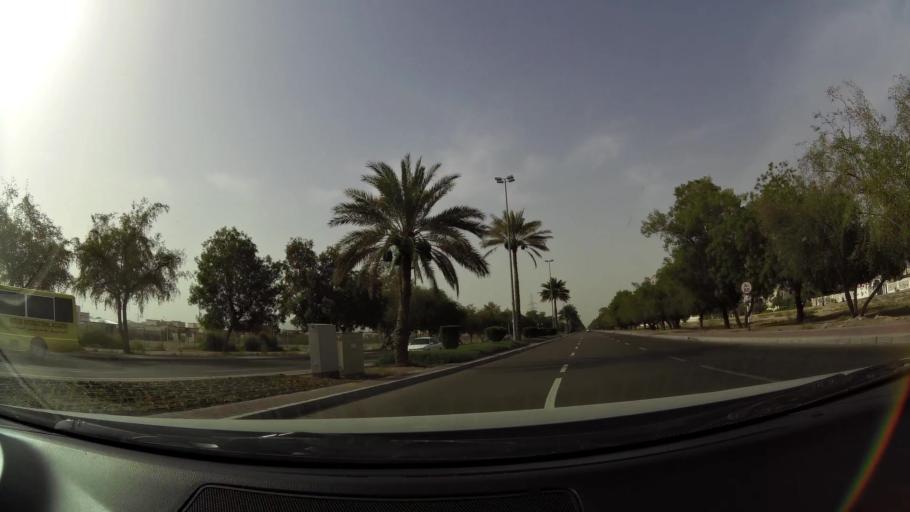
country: AE
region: Abu Dhabi
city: Al Ain
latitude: 24.1522
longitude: 55.7123
